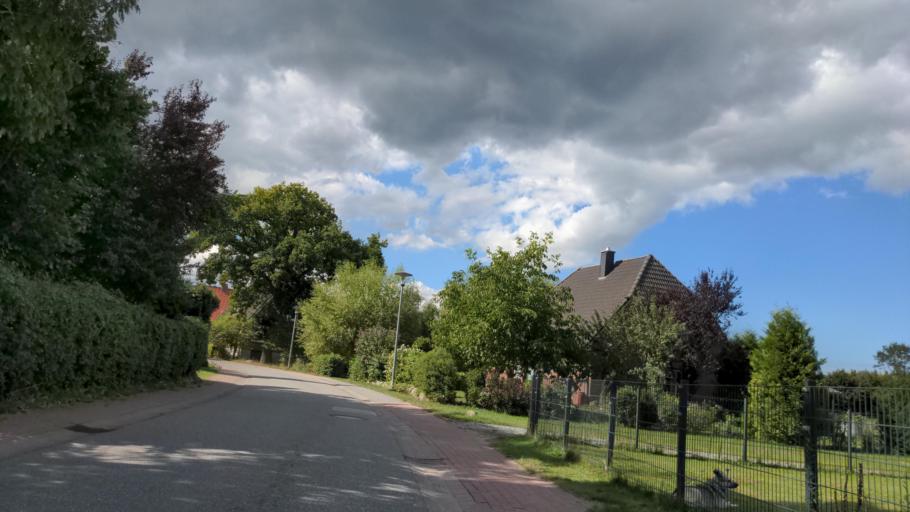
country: DE
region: Schleswig-Holstein
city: Kasseedorf
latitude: 54.1654
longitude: 10.7188
